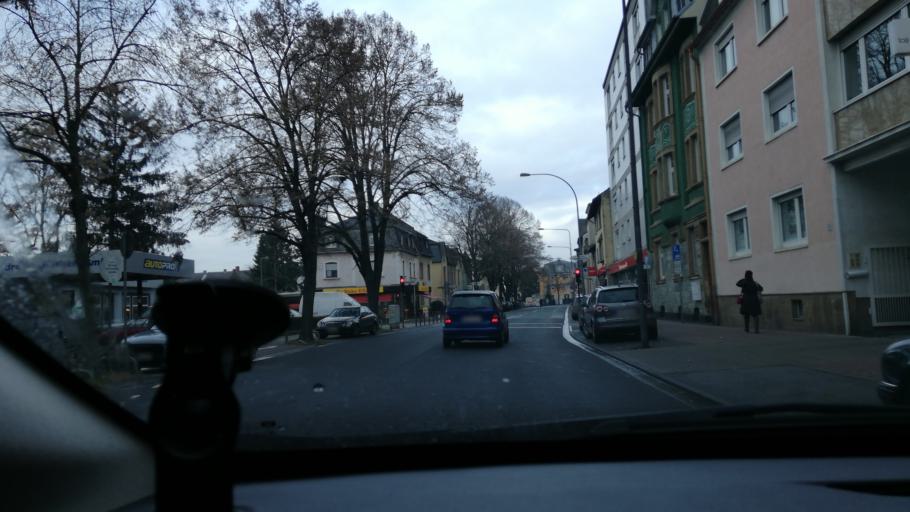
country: DE
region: Hesse
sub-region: Regierungsbezirk Darmstadt
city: Frankfurt am Main
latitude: 50.1507
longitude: 8.6913
